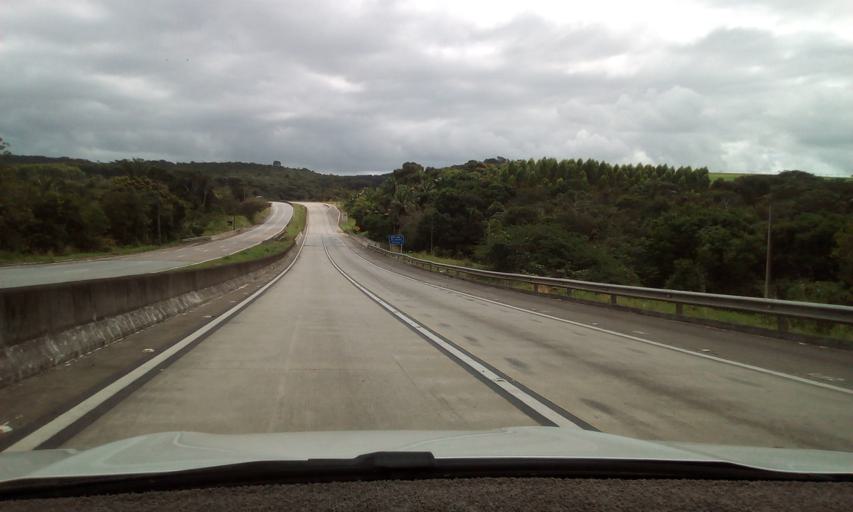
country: BR
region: Paraiba
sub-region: Cruz Do Espirito Santo
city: Cruz do Espirito Santo
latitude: -7.0139
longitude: -35.0611
